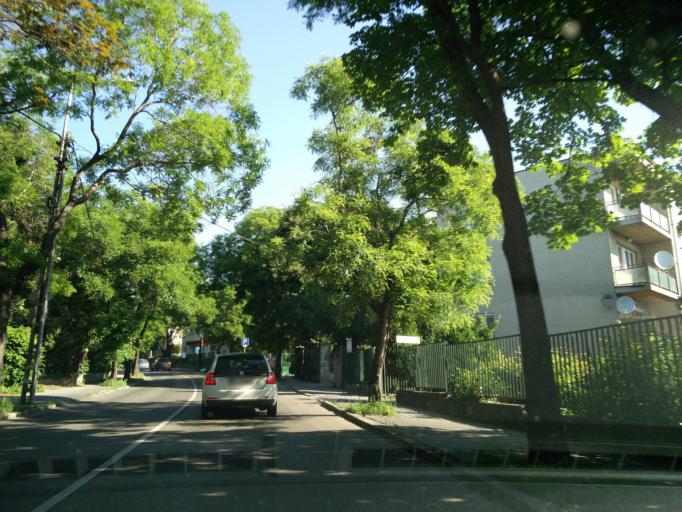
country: HU
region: Budapest
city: Budapest XII. keruelet
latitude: 47.5002
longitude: 19.0082
